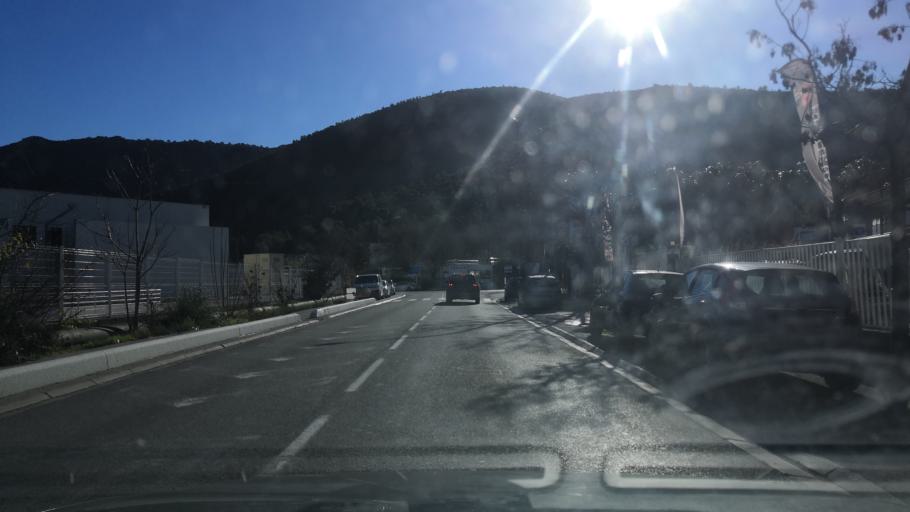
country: FR
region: Provence-Alpes-Cote d'Azur
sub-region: Departement des Bouches-du-Rhone
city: Gemenos
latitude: 43.2850
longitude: 5.6019
